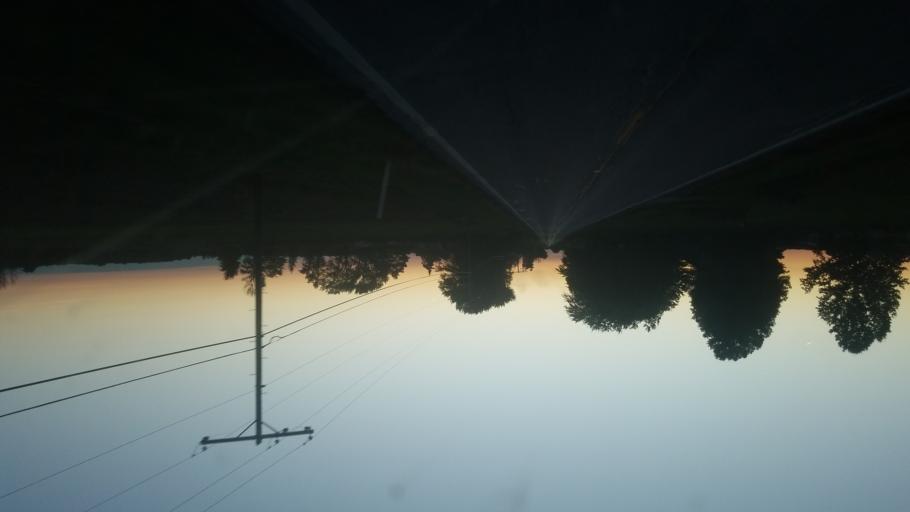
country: US
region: Ohio
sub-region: Ashtabula County
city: Jefferson
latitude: 41.7521
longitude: -80.6341
